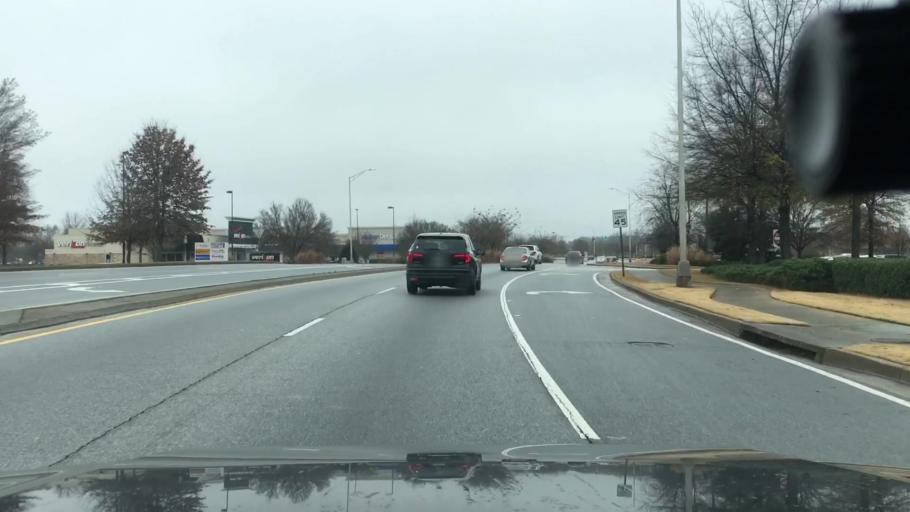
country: US
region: Georgia
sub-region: Coweta County
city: Newnan
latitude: 33.3935
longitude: -84.7613
